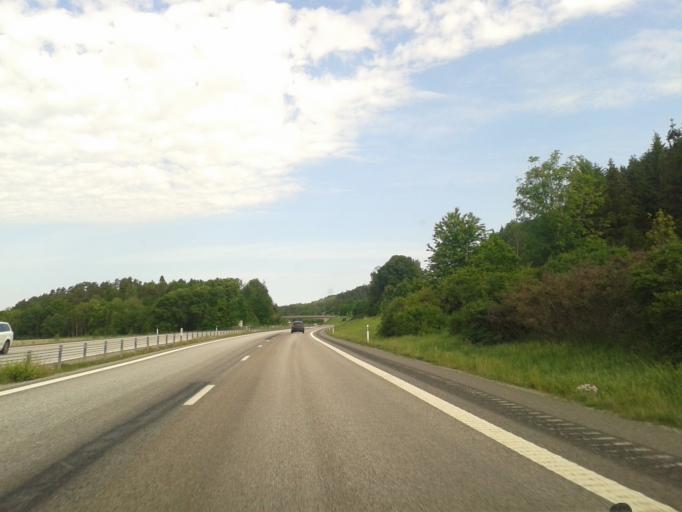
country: SE
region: Vaestra Goetaland
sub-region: Munkedals Kommun
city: Munkedal
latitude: 58.5373
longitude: 11.5298
